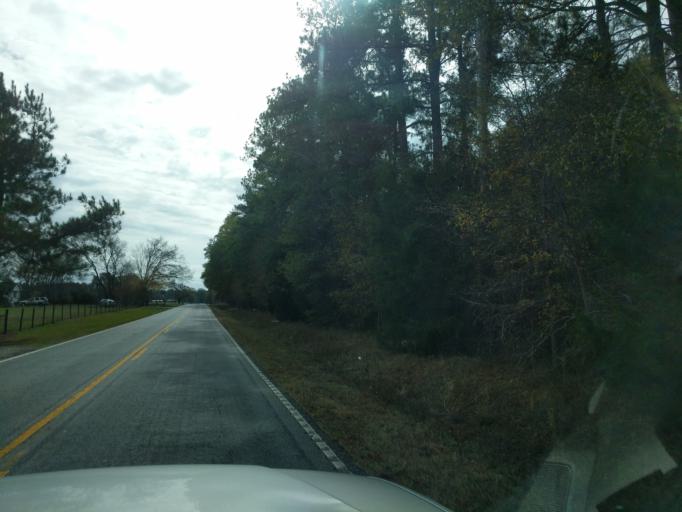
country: US
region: South Carolina
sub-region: Laurens County
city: Joanna
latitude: 34.3573
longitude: -81.8601
